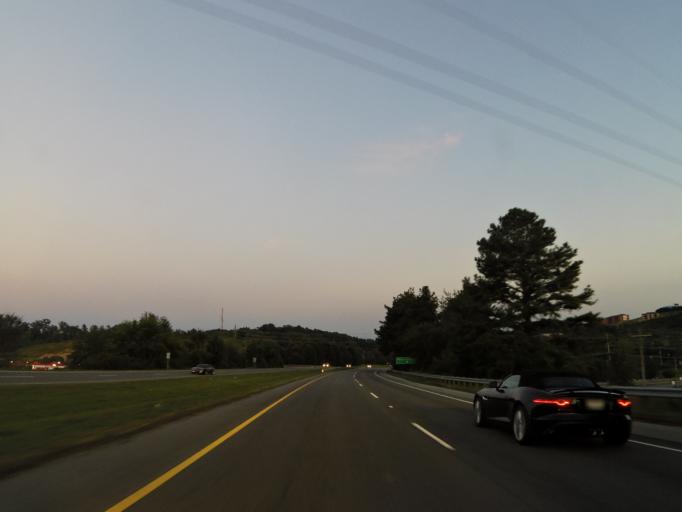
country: US
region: Tennessee
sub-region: Knox County
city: Farragut
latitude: 35.9511
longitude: -84.1586
